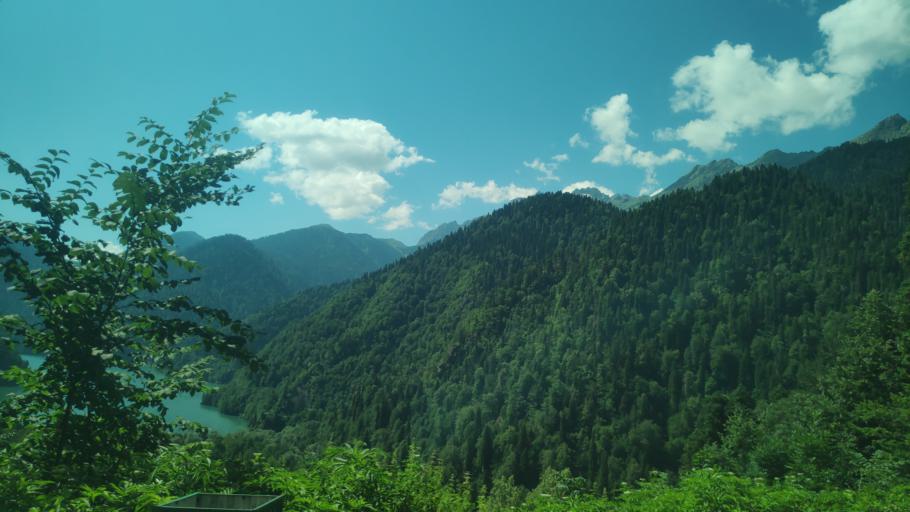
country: GE
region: Abkhazia
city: Gagra
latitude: 43.4792
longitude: 40.5688
